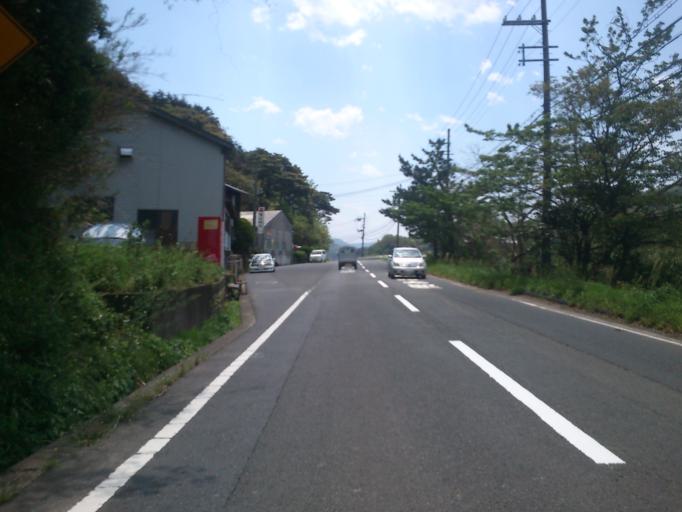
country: JP
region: Kyoto
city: Miyazu
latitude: 35.7276
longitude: 135.1037
